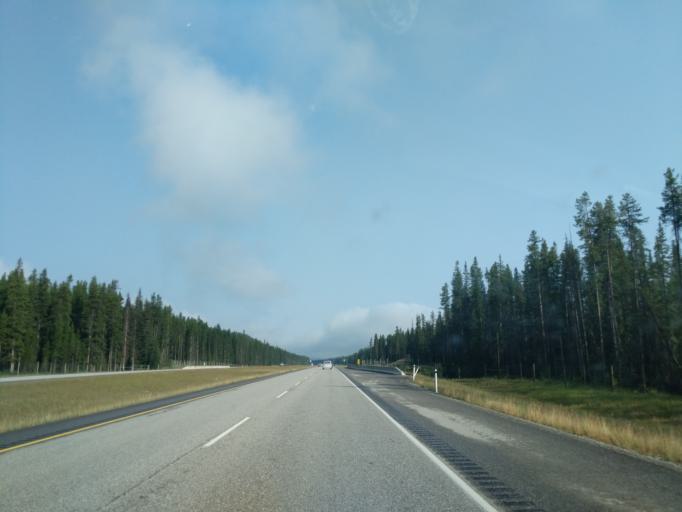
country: CA
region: Alberta
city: Lake Louise
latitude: 51.3351
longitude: -116.0585
